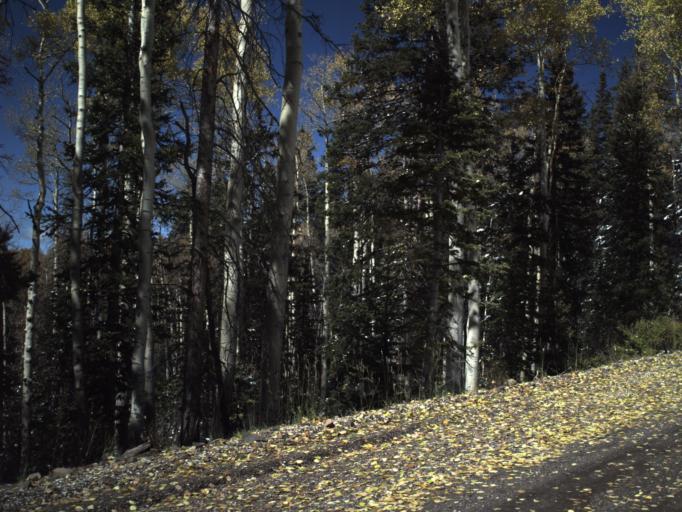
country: US
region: Utah
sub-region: Piute County
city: Junction
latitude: 38.2592
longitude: -112.3788
